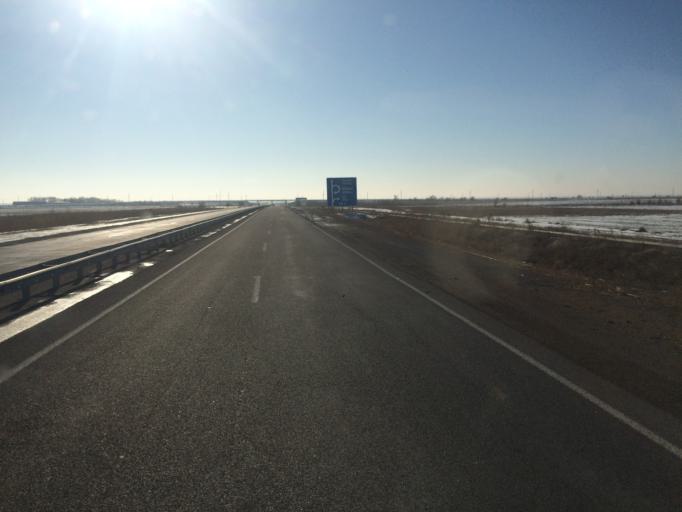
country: KG
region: Chuy
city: Sokuluk
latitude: 43.2832
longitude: 74.2371
